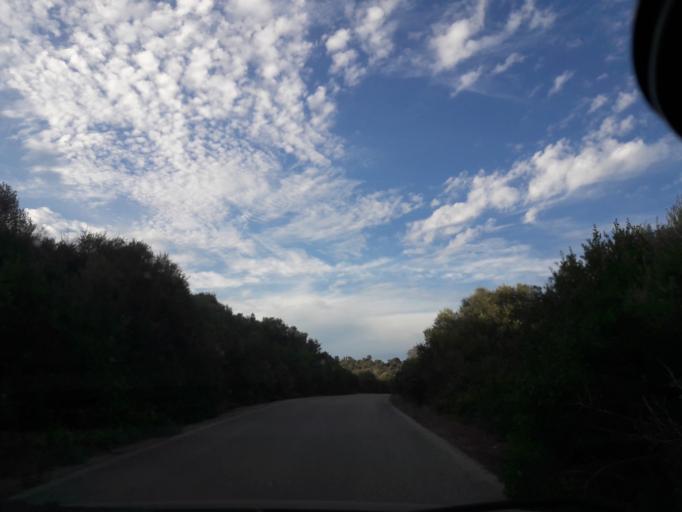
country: GR
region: Central Macedonia
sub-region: Nomos Chalkidikis
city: Nea Roda
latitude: 40.3311
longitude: 23.8980
